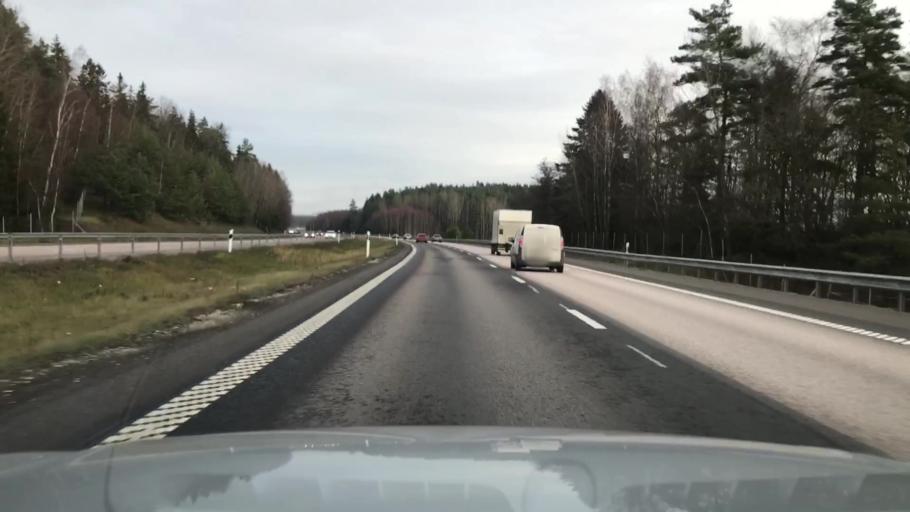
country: SE
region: Stockholm
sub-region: Sodertalje Kommun
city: Pershagen
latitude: 59.0580
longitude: 17.5777
